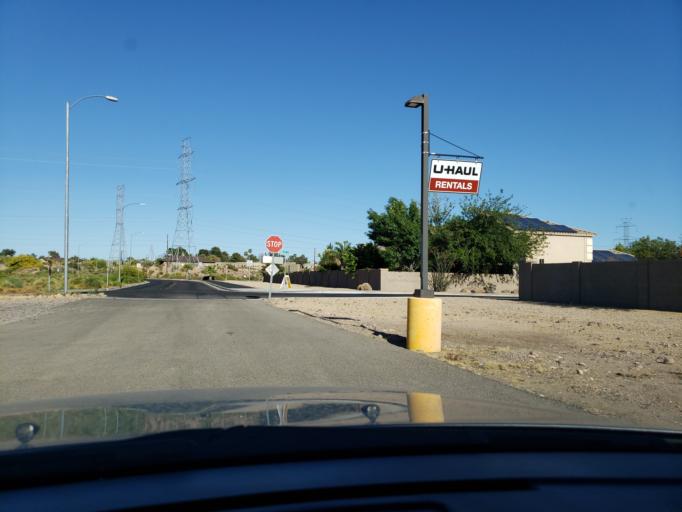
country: US
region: Arizona
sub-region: Maricopa County
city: Youngtown
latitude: 33.5799
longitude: -112.3096
